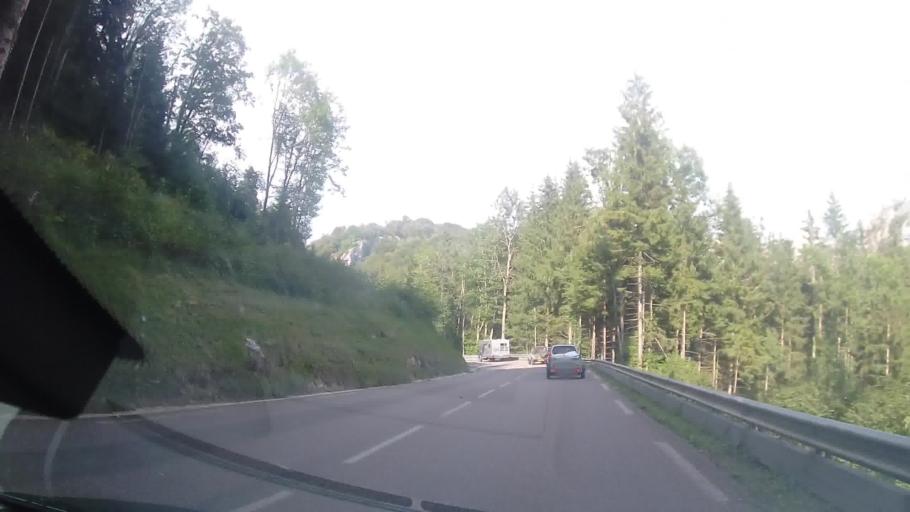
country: FR
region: Franche-Comte
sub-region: Departement du Jura
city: Champagnole
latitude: 46.6092
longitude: 5.8969
